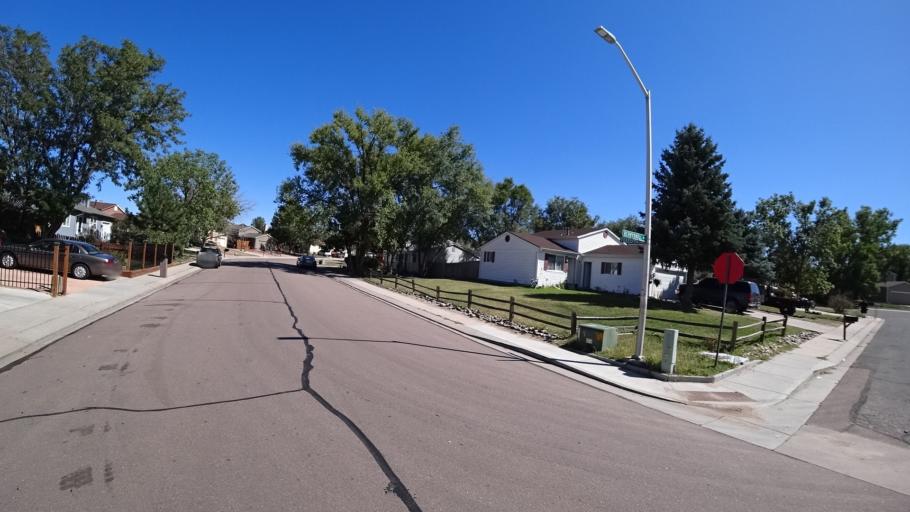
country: US
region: Colorado
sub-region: El Paso County
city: Stratmoor
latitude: 38.7864
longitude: -104.7438
